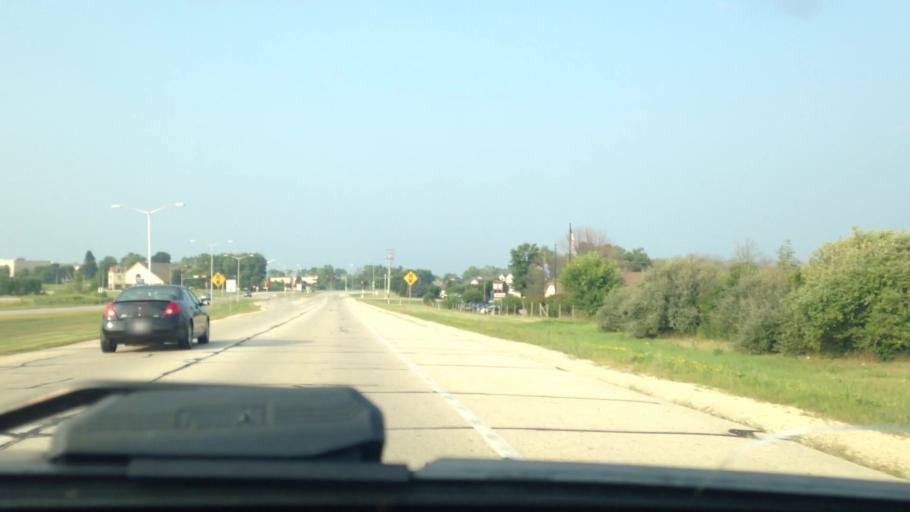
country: US
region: Wisconsin
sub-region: Washington County
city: Germantown
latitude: 43.2159
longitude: -88.1448
